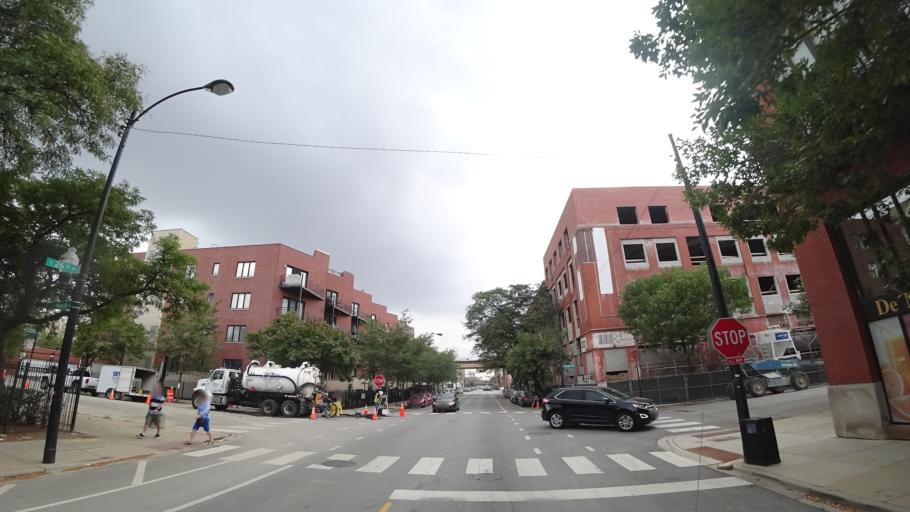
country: US
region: Illinois
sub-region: Cook County
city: Chicago
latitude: 41.8456
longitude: -87.6251
